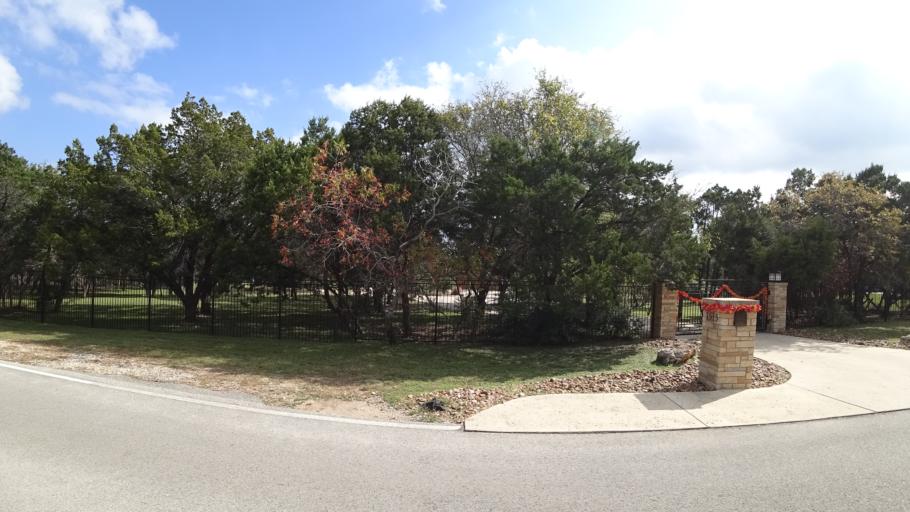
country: US
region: Texas
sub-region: Travis County
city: Barton Creek
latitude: 30.3007
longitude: -97.8709
